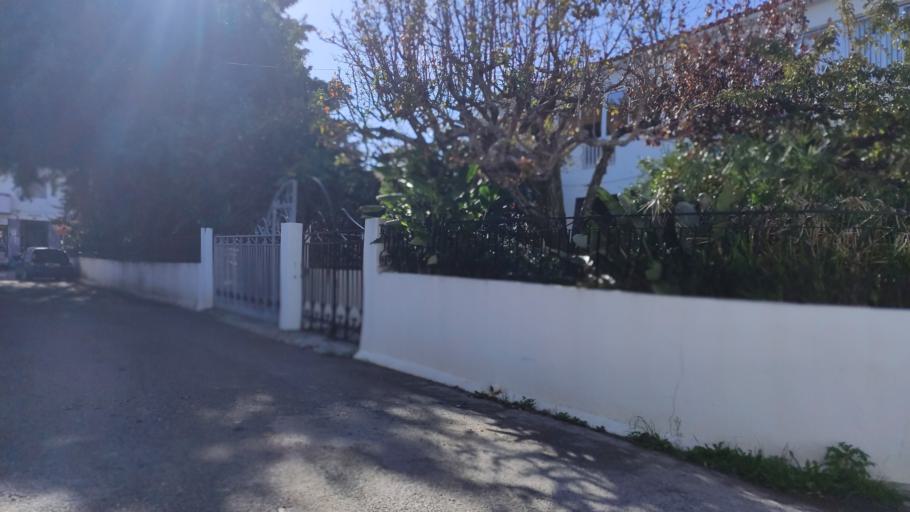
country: PT
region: Faro
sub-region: Sao Bras de Alportel
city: Sao Bras de Alportel
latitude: 37.1530
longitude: -7.8815
